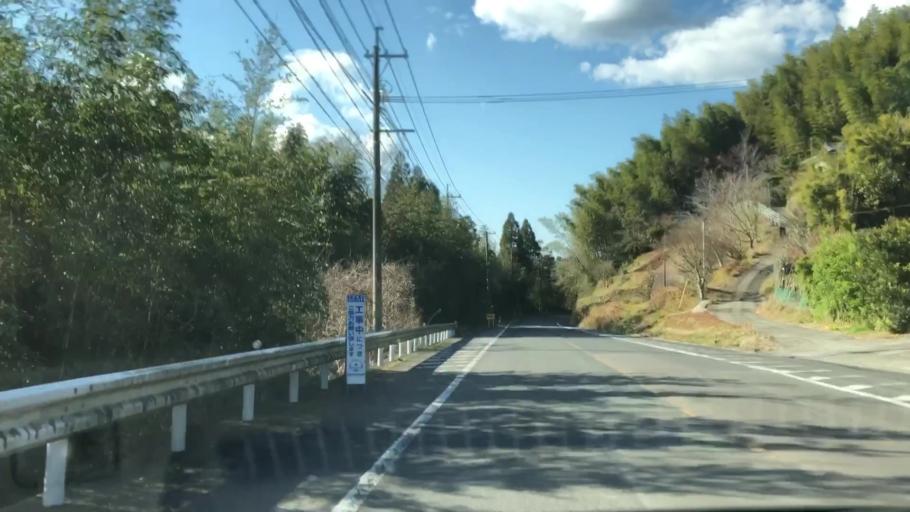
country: JP
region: Kagoshima
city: Satsumasendai
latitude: 31.8594
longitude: 130.4055
